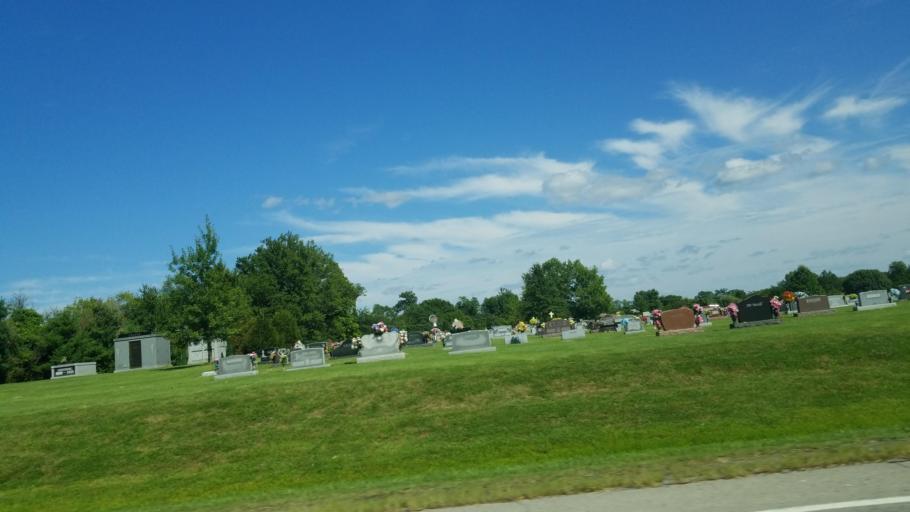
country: US
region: Illinois
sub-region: Williamson County
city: Marion
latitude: 37.7466
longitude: -88.9327
